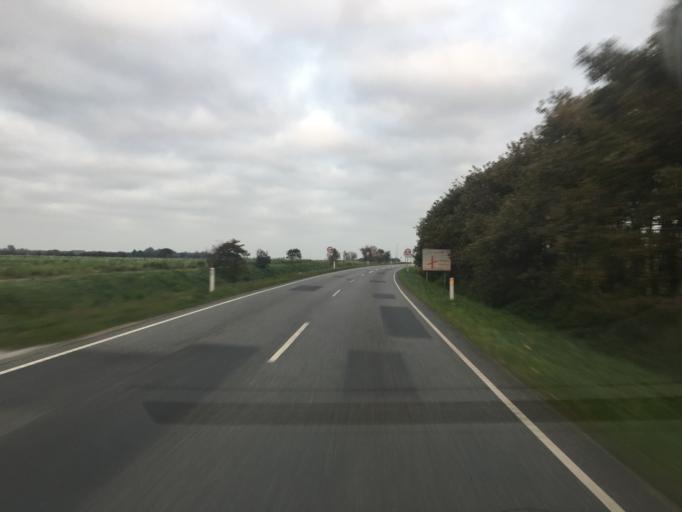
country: DE
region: Schleswig-Holstein
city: Aventoft
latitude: 54.9512
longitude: 8.7965
